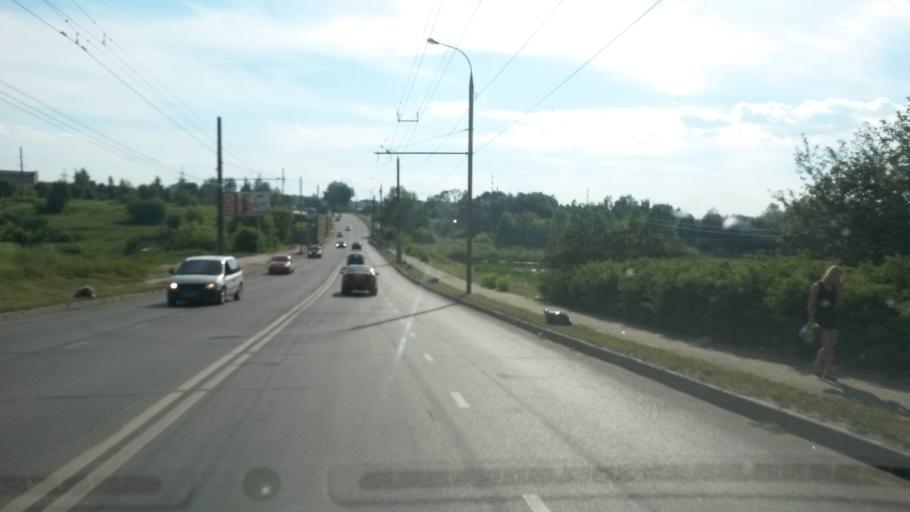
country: RU
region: Ivanovo
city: Kokhma
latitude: 56.9662
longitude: 41.0426
